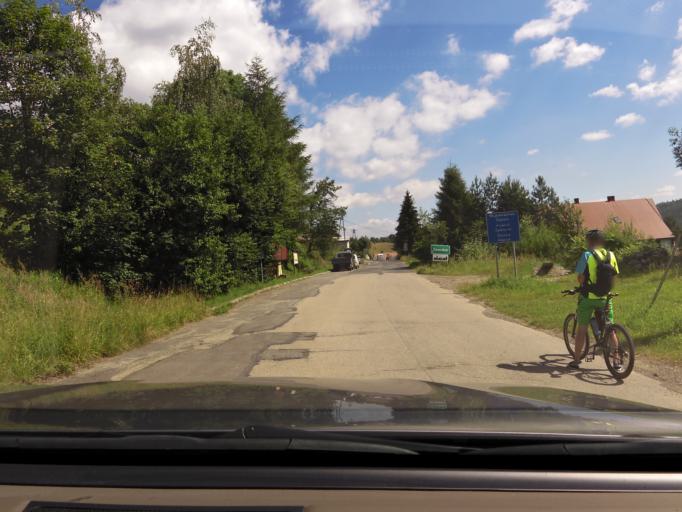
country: PL
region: Silesian Voivodeship
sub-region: Powiat cieszynski
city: Koniakow
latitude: 49.5101
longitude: 18.9633
